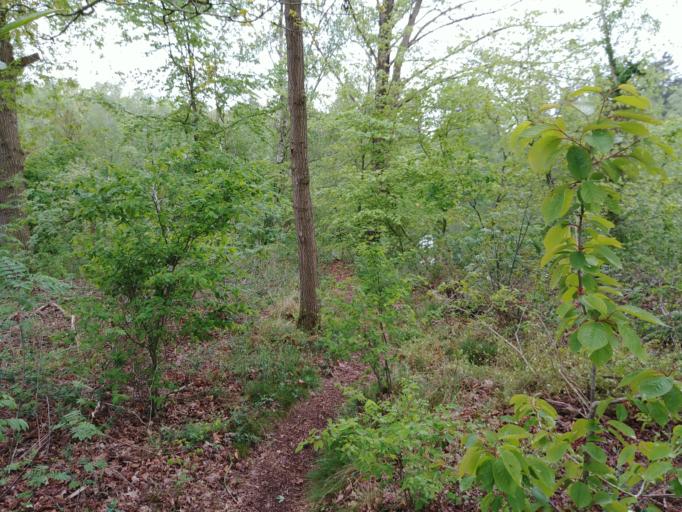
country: NL
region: Overijssel
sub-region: Gemeente Dalfsen
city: Dalfsen
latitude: 52.5182
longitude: 6.3583
